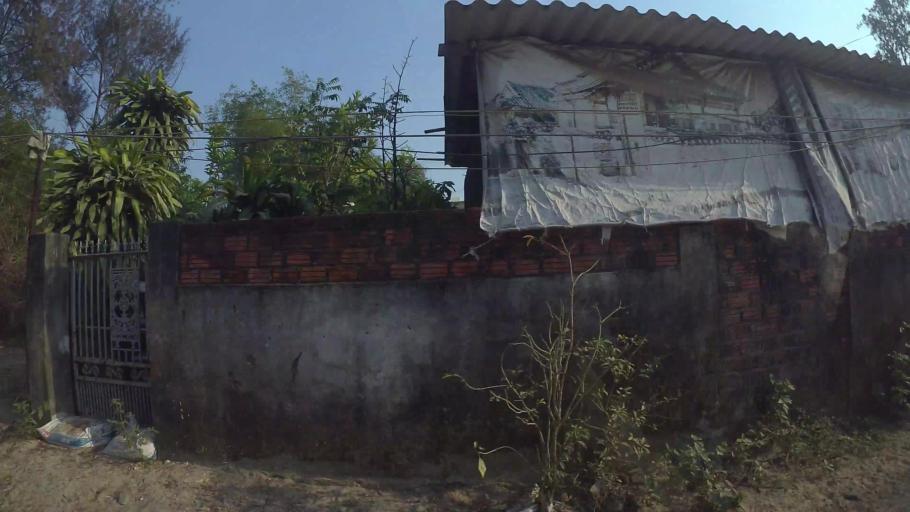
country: VN
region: Da Nang
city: Ngu Hanh Son
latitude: 15.9595
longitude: 108.2646
